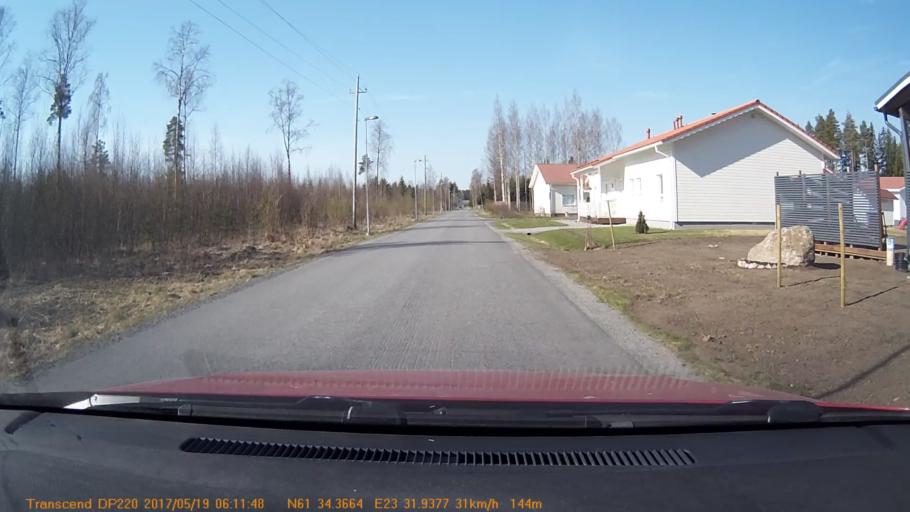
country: FI
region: Pirkanmaa
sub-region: Tampere
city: Yloejaervi
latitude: 61.5729
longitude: 23.5324
